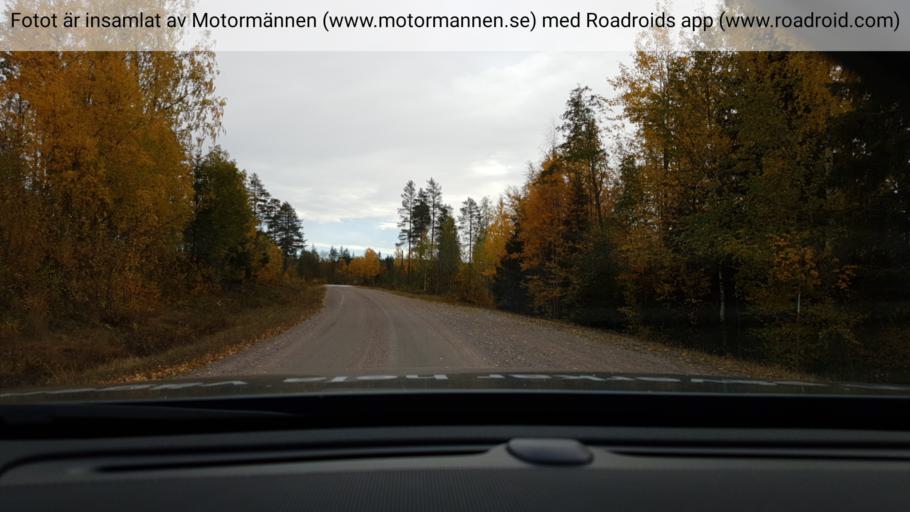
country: SE
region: Norrbotten
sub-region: Overkalix Kommun
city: OEverkalix
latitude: 66.2612
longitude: 23.0281
